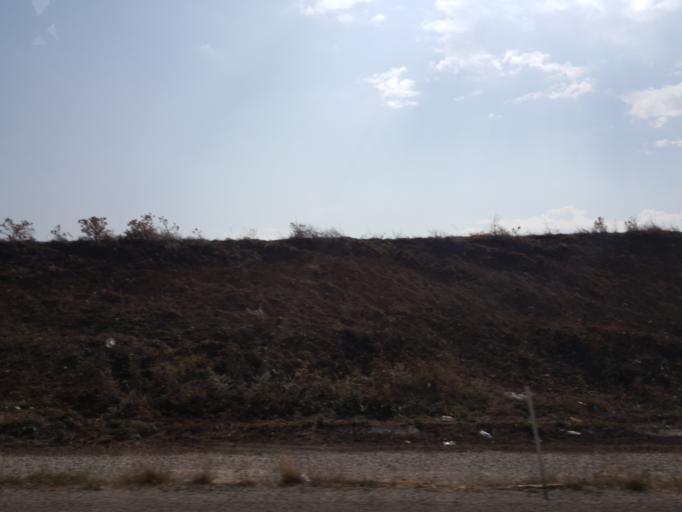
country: TR
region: Corum
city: Alaca
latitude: 40.1457
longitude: 34.8359
